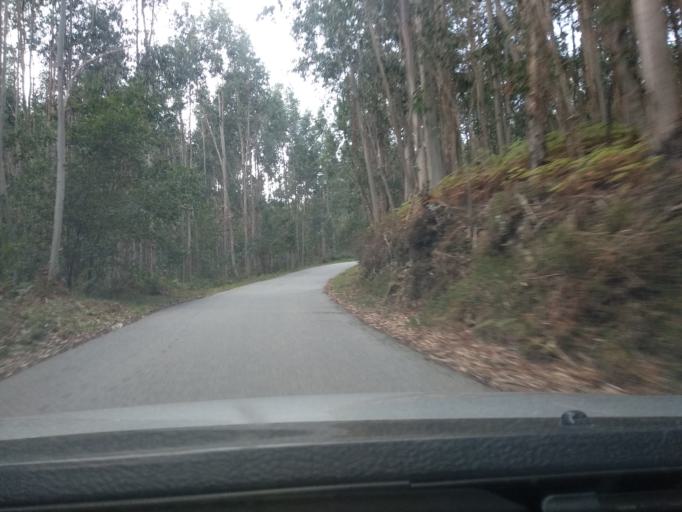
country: ES
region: Galicia
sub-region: Provincia de Pontevedra
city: Moana
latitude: 42.2962
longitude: -8.6942
